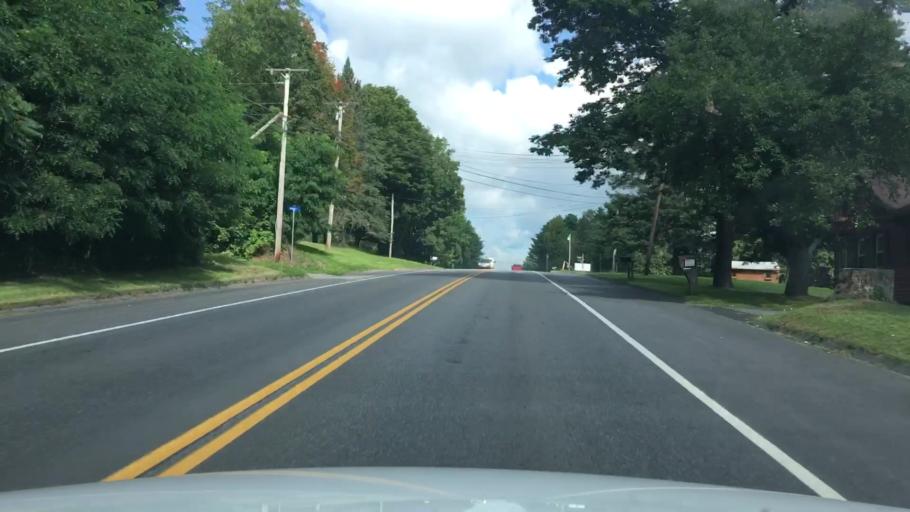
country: US
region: Maine
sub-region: Kennebec County
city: Waterville
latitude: 44.6111
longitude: -69.6654
